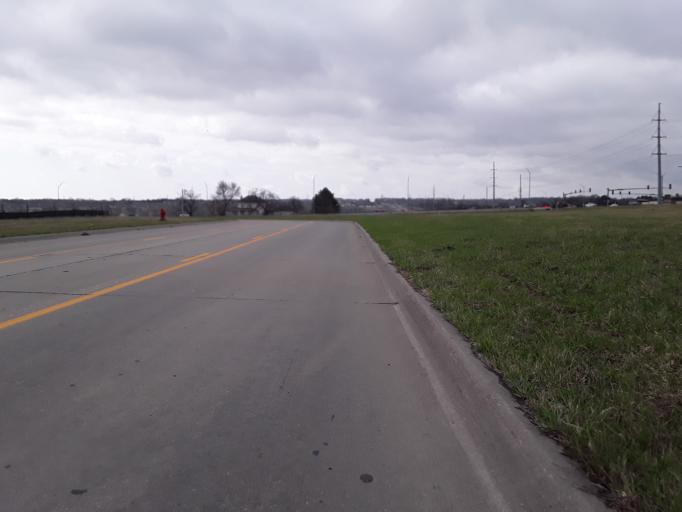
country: US
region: Nebraska
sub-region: Lancaster County
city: Lincoln
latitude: 40.8444
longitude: -96.6046
